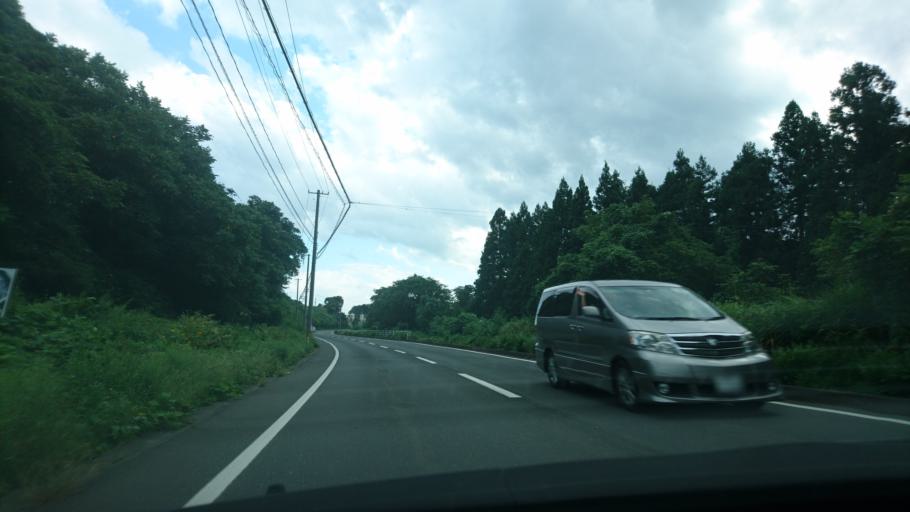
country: JP
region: Iwate
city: Kitakami
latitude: 39.2561
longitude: 141.1222
